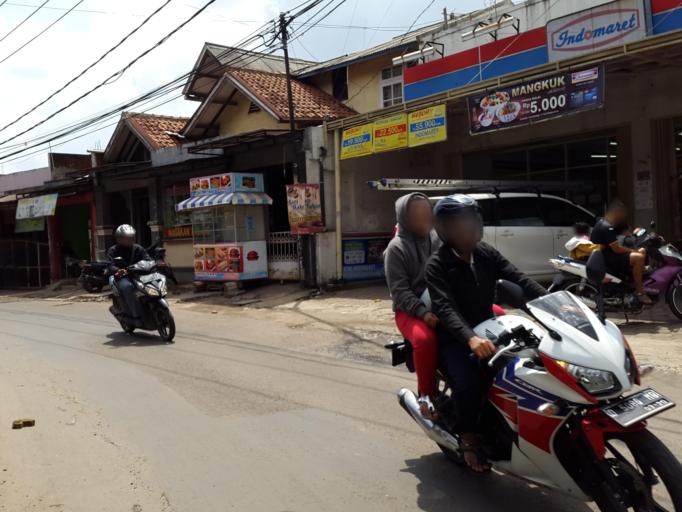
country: ID
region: West Java
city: Bandung
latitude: -6.8898
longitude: 107.6643
